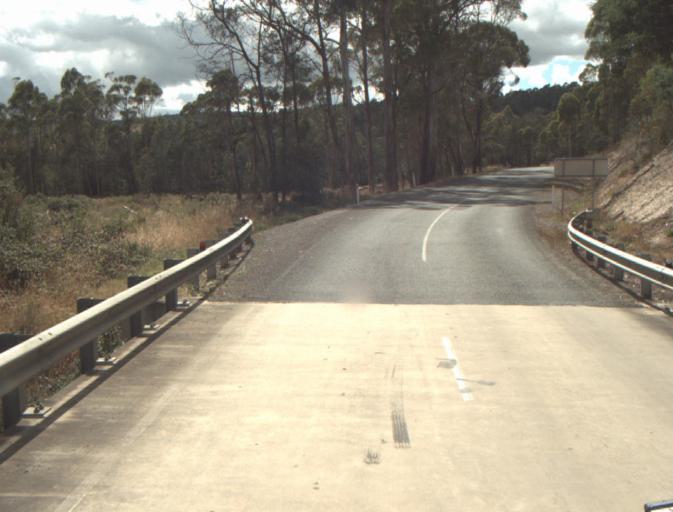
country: AU
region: Tasmania
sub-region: Launceston
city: Mayfield
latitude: -41.2092
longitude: 147.1266
